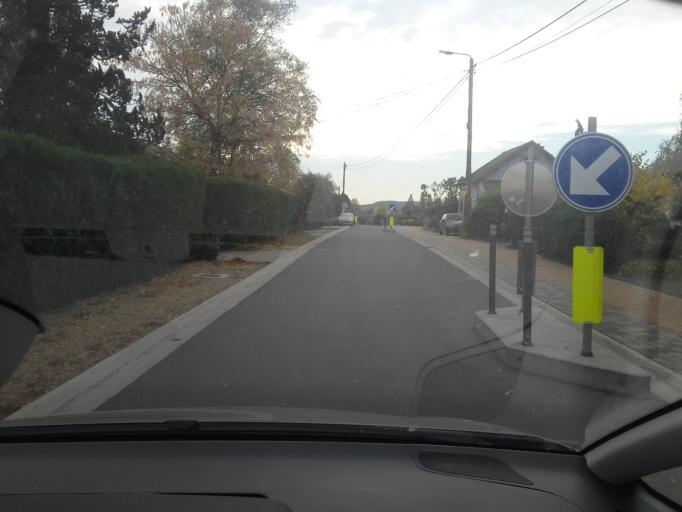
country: BE
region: Wallonia
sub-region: Province du Luxembourg
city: Arlon
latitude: 49.6982
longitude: 5.8182
